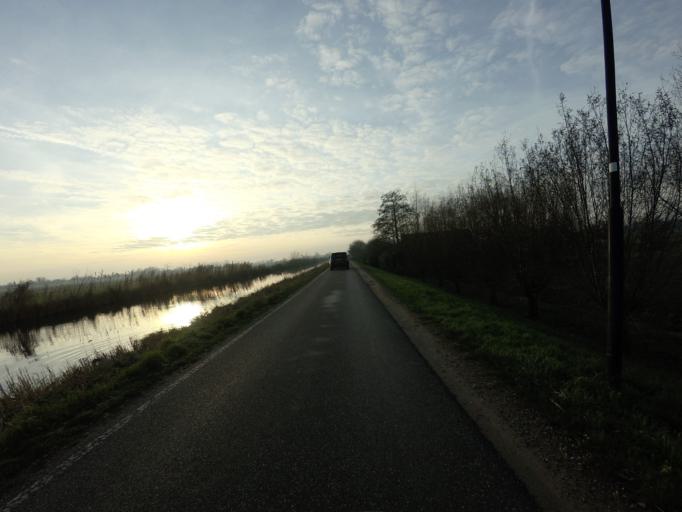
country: NL
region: Utrecht
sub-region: Gemeente De Ronde Venen
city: Mijdrecht
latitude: 52.1666
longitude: 4.9257
